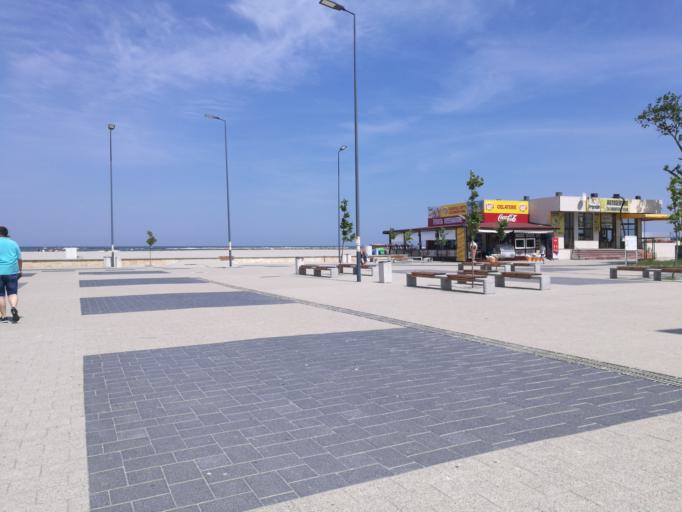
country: RO
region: Constanta
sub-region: Municipiul Constanta
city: Palazu Mare
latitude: 44.2215
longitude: 28.6337
